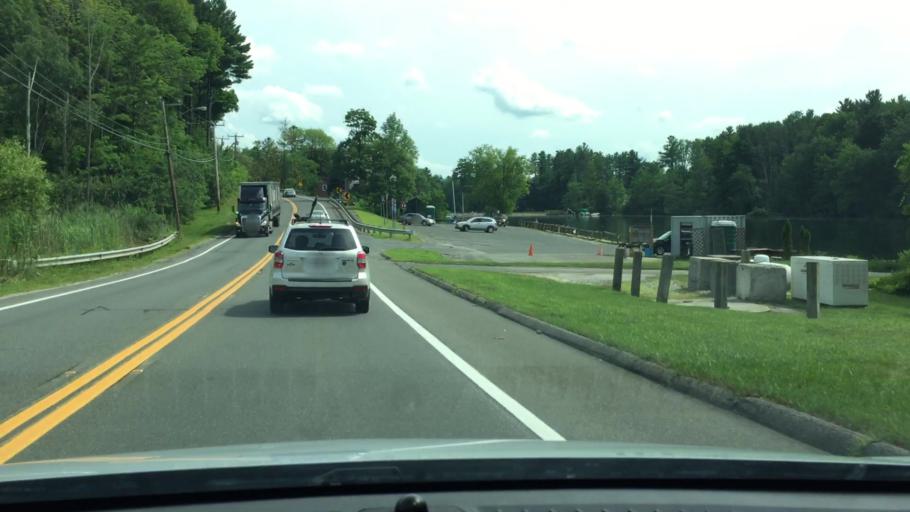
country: US
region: Massachusetts
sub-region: Berkshire County
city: Lee
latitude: 42.3251
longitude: -73.2613
